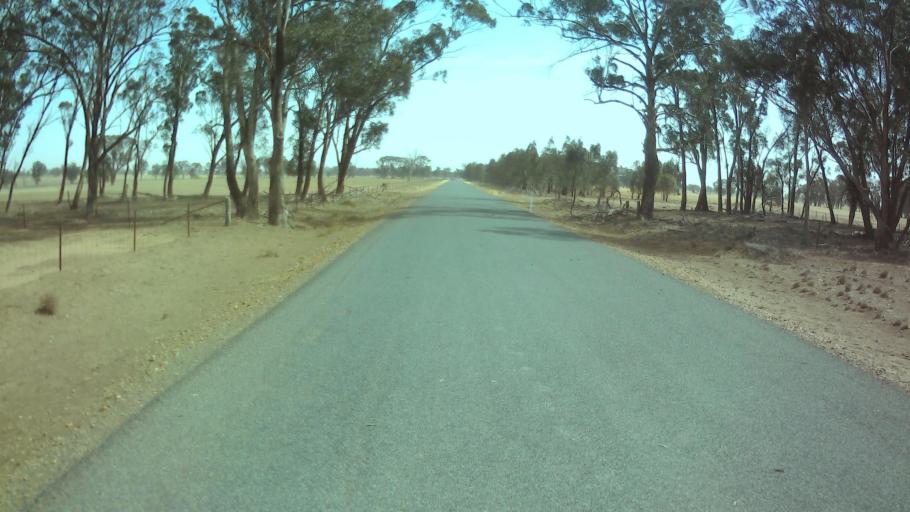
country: AU
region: New South Wales
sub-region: Weddin
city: Grenfell
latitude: -33.7156
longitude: 148.0008
